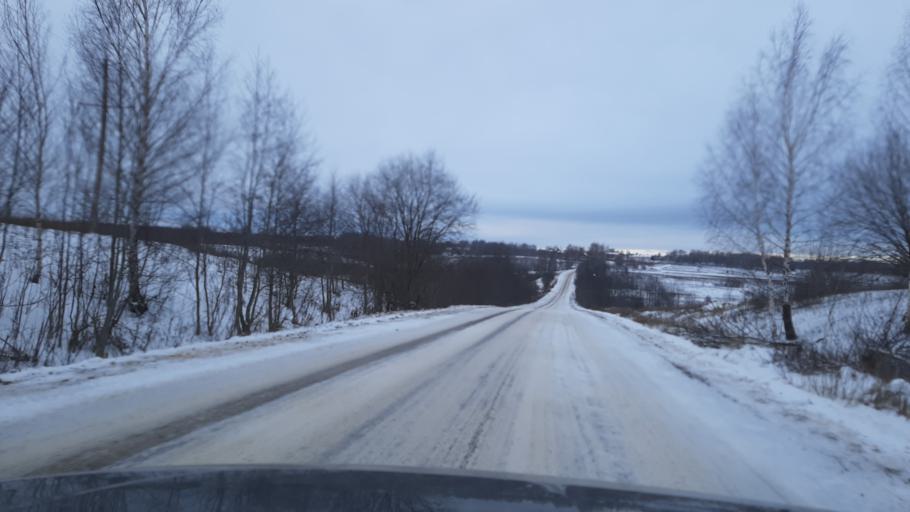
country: RU
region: Kostroma
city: Volgorechensk
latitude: 57.4379
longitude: 41.0887
